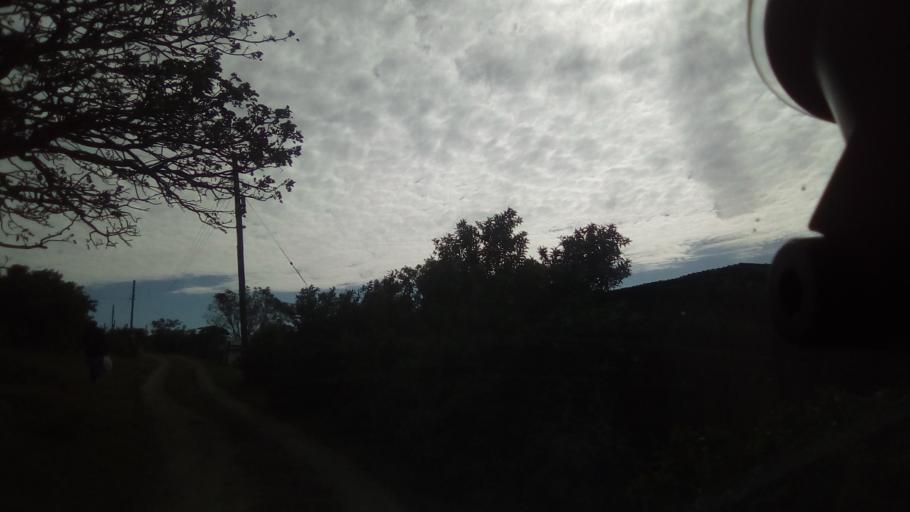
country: ZA
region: Eastern Cape
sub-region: Buffalo City Metropolitan Municipality
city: East London
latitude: -32.7958
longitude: 27.9571
